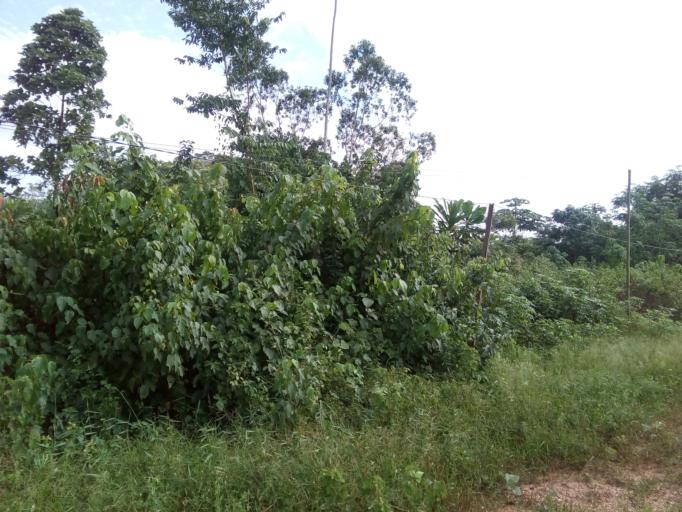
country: CI
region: Sud-Comoe
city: Tiapoum
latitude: 5.2733
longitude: -2.7917
